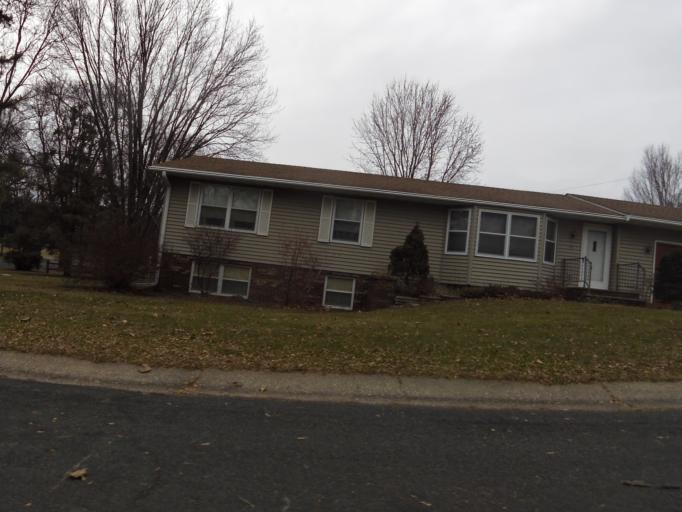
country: US
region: Wisconsin
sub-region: Pierce County
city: River Falls
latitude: 44.8617
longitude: -92.6104
